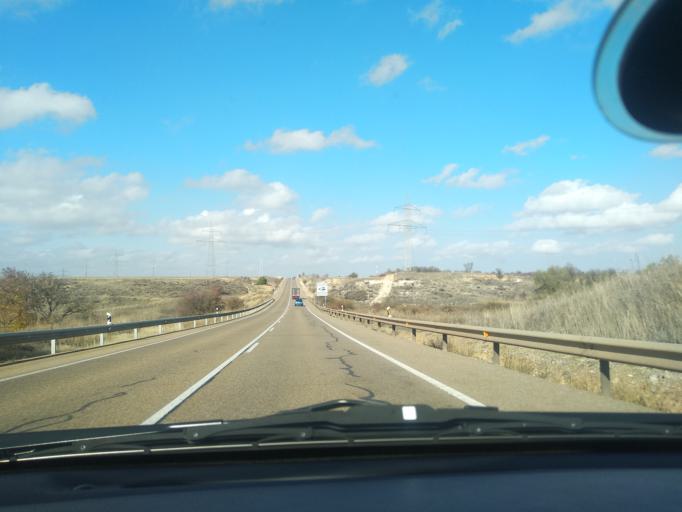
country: ES
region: Castille and Leon
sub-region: Provincia de Valladolid
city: Valverde de Campos
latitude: 41.8257
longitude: -5.0005
